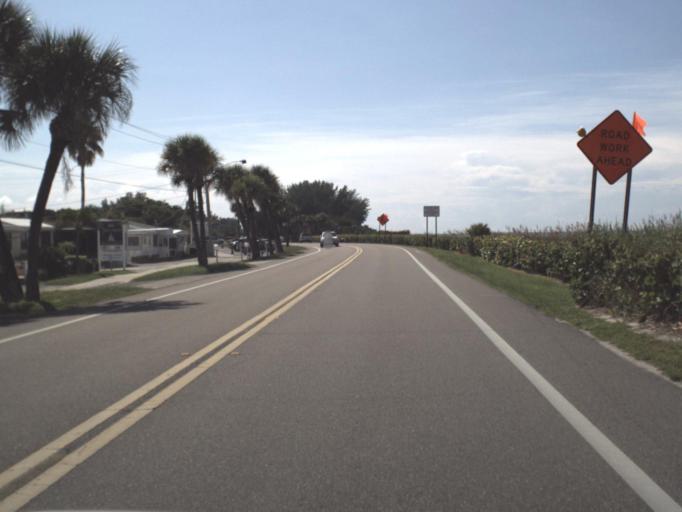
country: US
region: Florida
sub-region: Manatee County
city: Longboat Key
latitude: 27.3822
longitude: -82.6377
